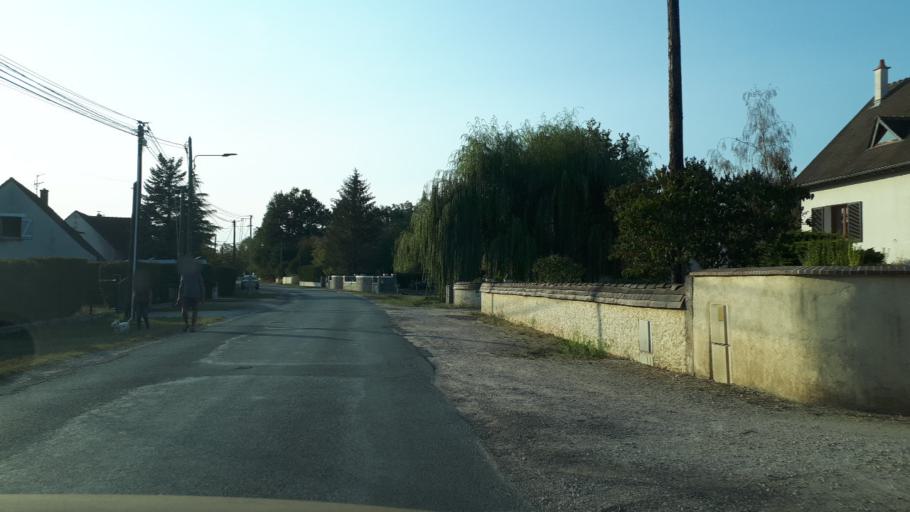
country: FR
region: Centre
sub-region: Departement du Loir-et-Cher
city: Romorantin-Lanthenay
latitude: 47.3439
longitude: 1.7701
